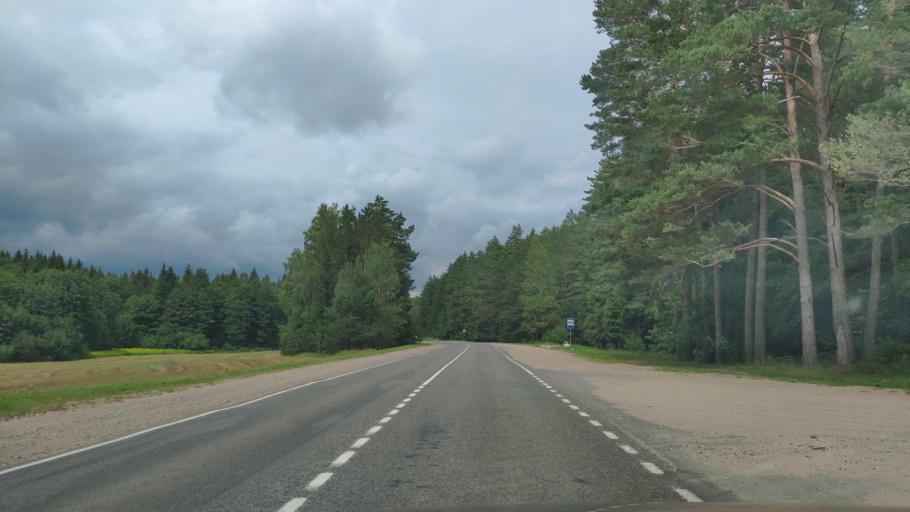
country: BY
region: Minsk
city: Zaslawye
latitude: 53.9706
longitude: 27.2475
